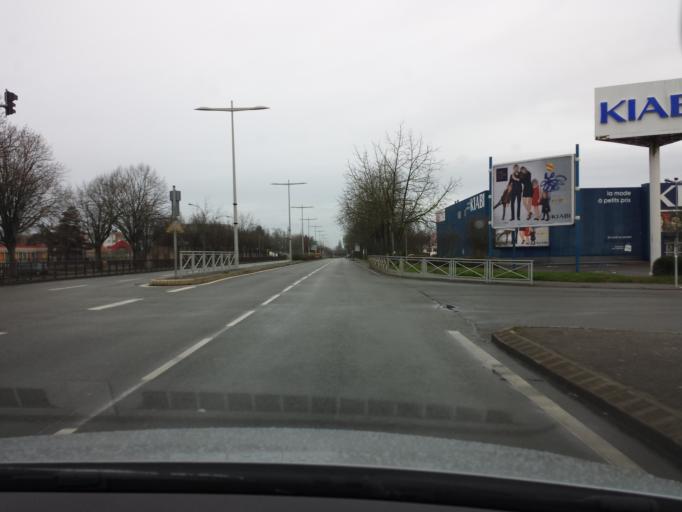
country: FR
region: Haute-Normandie
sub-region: Departement de l'Eure
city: Evreux
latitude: 49.0116
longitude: 1.1683
